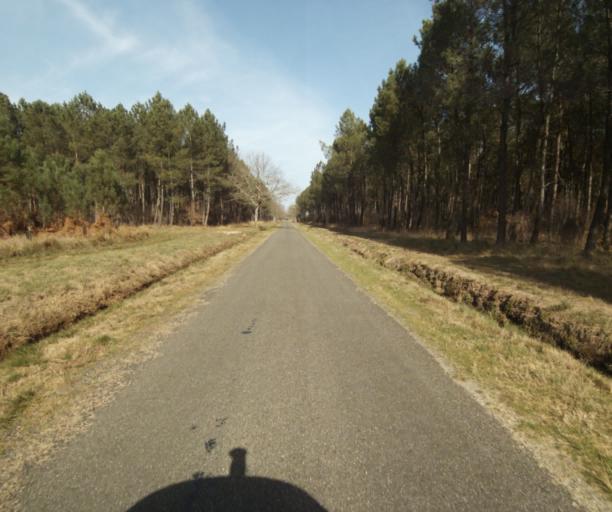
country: FR
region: Aquitaine
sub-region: Departement de la Gironde
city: Bazas
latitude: 44.2206
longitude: -0.2049
